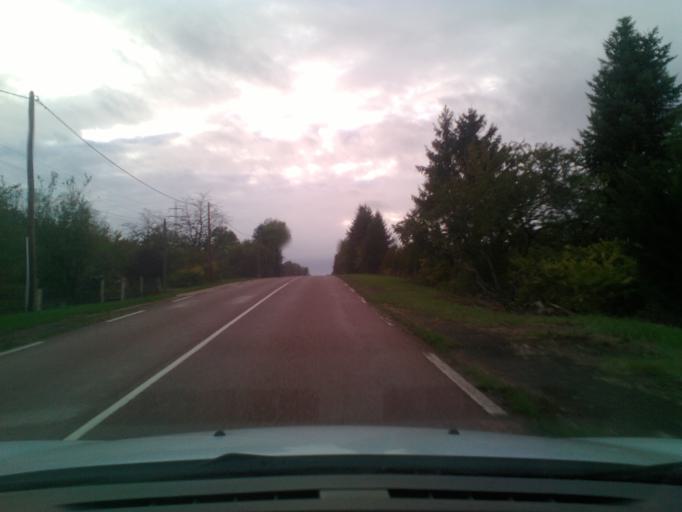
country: FR
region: Lorraine
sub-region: Departement des Vosges
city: Chatel-sur-Moselle
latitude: 48.3489
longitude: 6.4099
